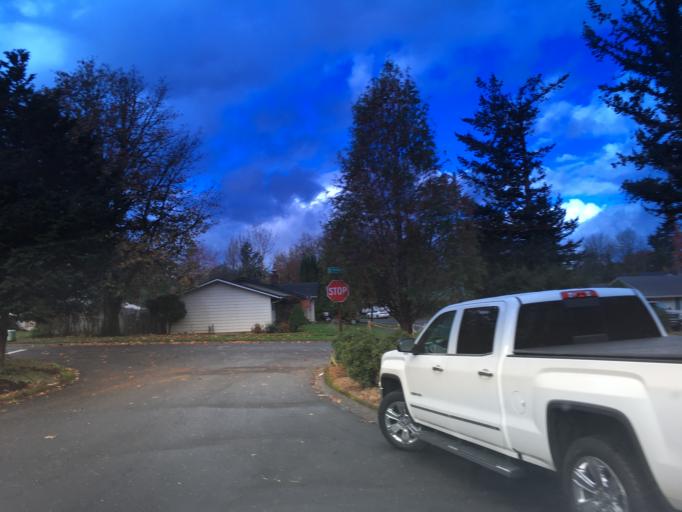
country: US
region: Oregon
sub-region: Multnomah County
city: Troutdale
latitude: 45.5147
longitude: -122.3770
